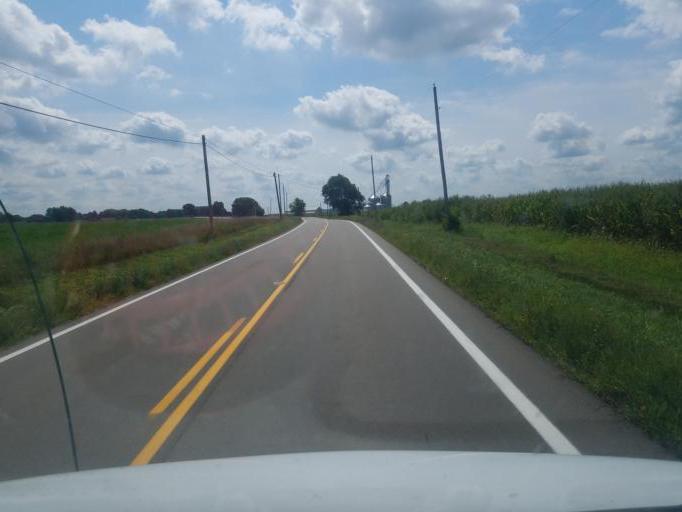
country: US
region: Ohio
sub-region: Marion County
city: Prospect
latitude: 40.3978
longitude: -83.1622
